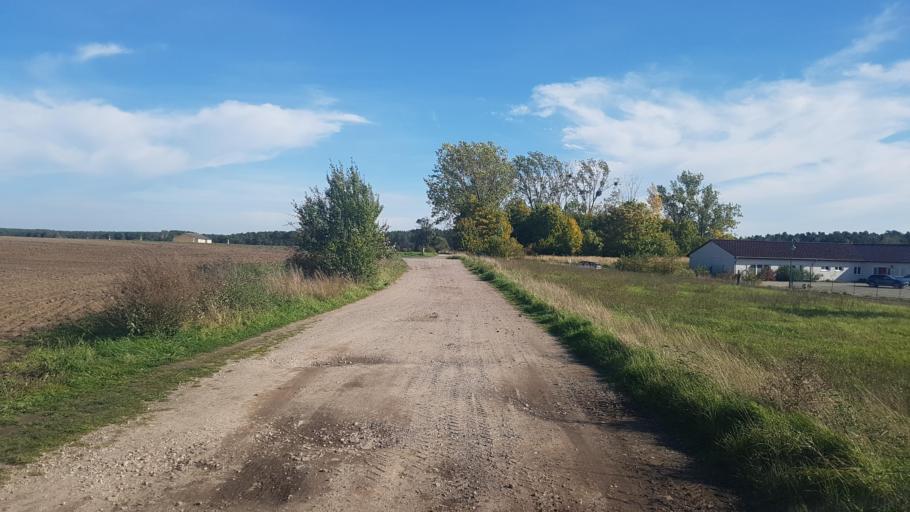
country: DE
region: Saxony-Anhalt
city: Nudersdorf
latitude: 51.9561
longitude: 12.6013
